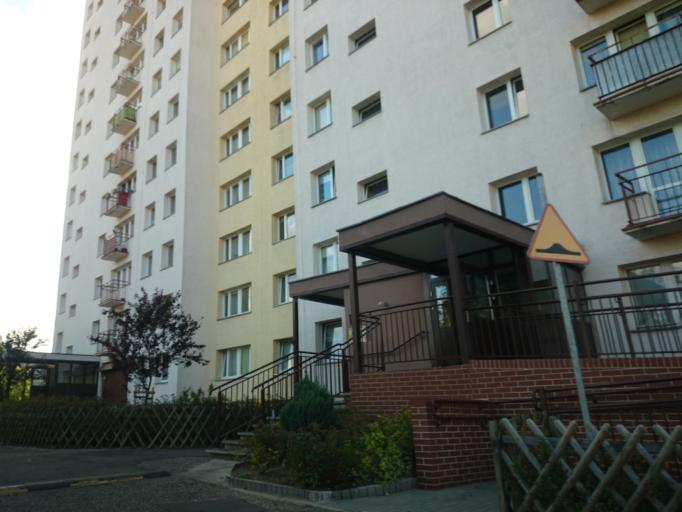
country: PL
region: West Pomeranian Voivodeship
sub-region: Szczecin
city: Szczecin
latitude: 53.3781
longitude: 14.6602
